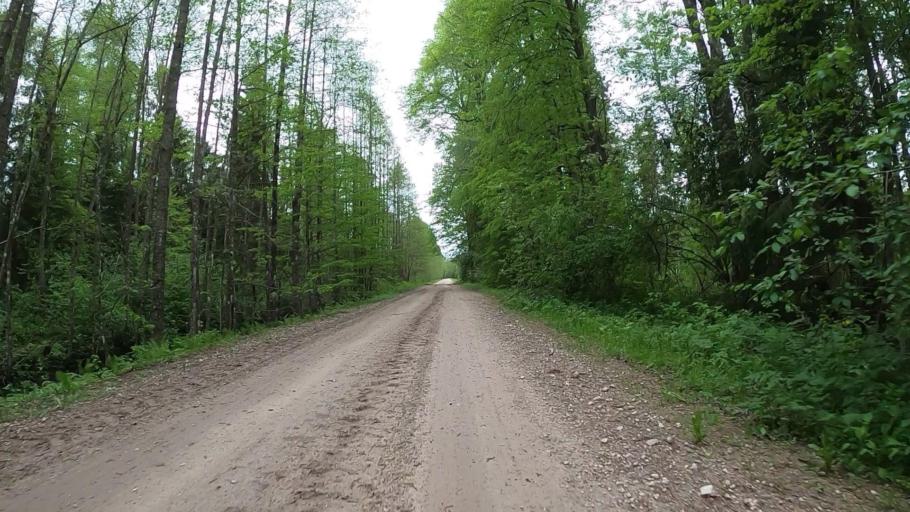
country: LV
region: Ozolnieku
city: Ozolnieki
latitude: 56.7916
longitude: 23.7768
